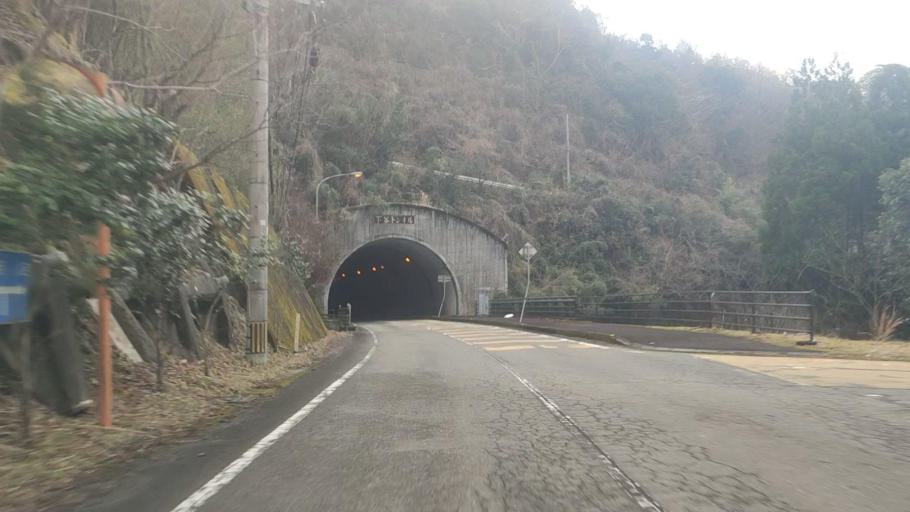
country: JP
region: Kumamoto
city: Hitoyoshi
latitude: 32.3835
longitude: 130.8348
